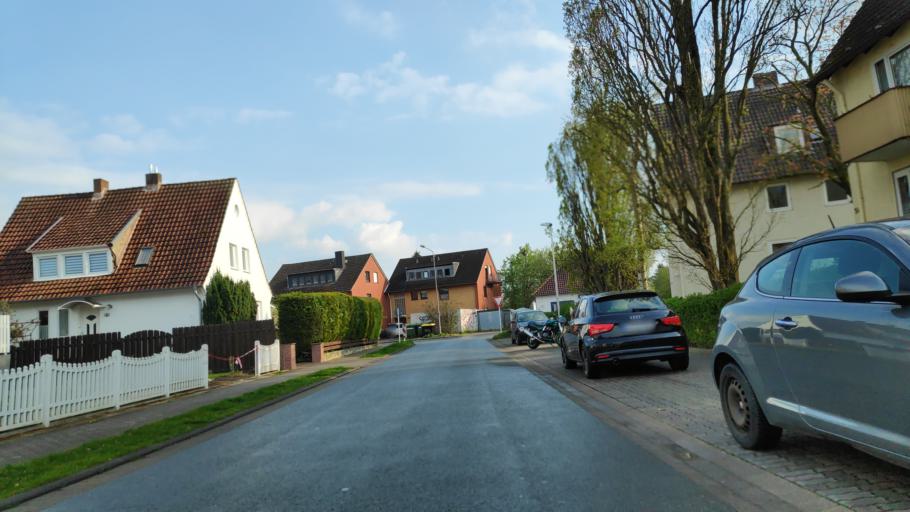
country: DE
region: North Rhine-Westphalia
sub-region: Regierungsbezirk Detmold
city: Minden
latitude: 52.2890
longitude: 8.9491
